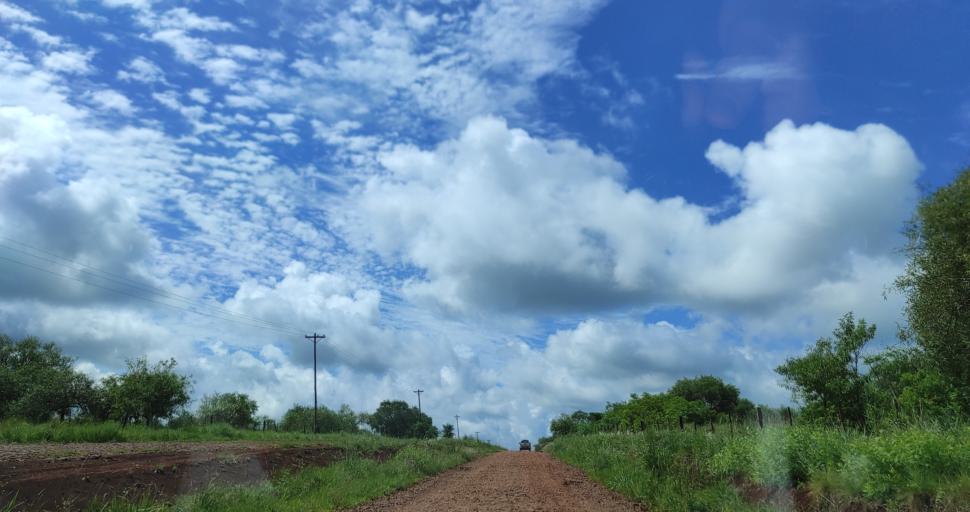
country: AR
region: Misiones
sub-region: Departamento de Apostoles
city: San Jose
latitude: -27.7608
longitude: -55.7887
